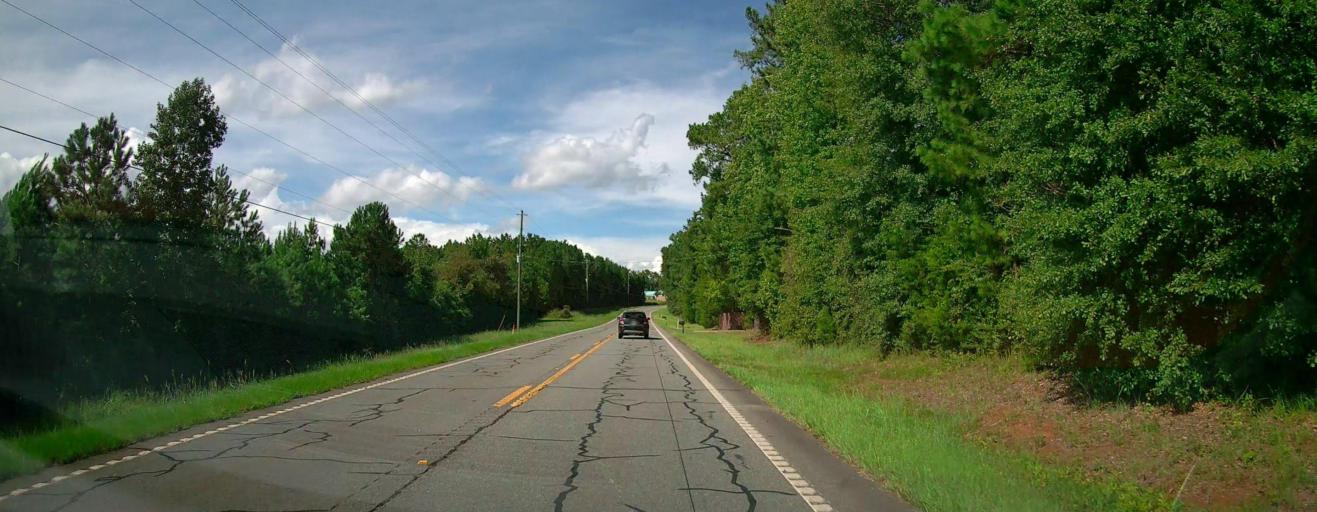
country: US
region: Georgia
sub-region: Talbot County
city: Sardis
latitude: 32.7647
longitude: -84.5583
